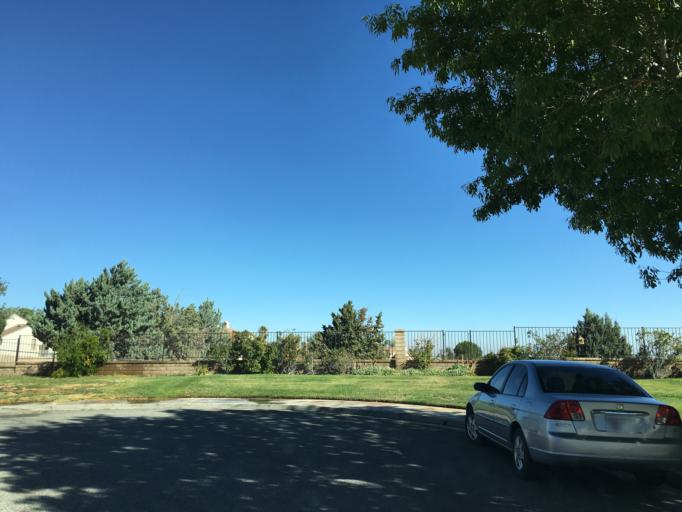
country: US
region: California
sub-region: Los Angeles County
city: Desert View Highlands
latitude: 34.5844
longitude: -118.1557
